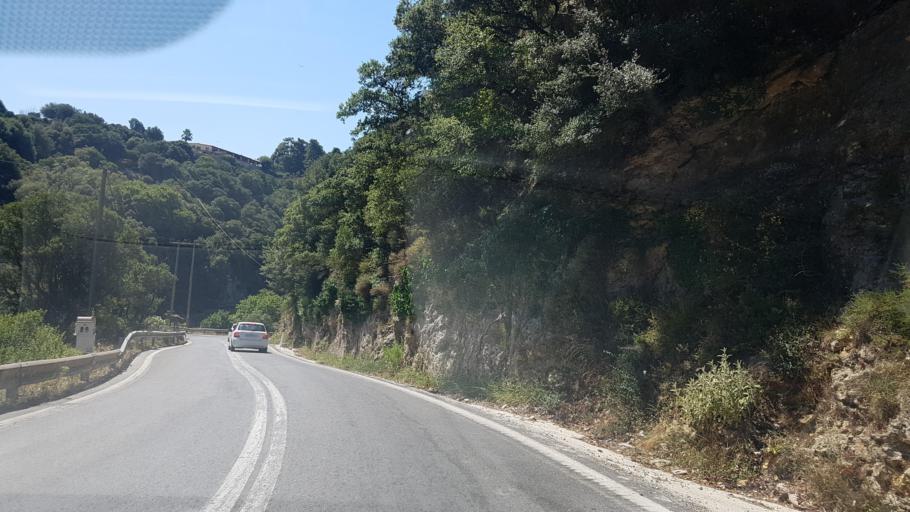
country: GR
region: Crete
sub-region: Nomos Rethymnis
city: Agia Foteini
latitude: 35.3130
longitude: 24.6260
